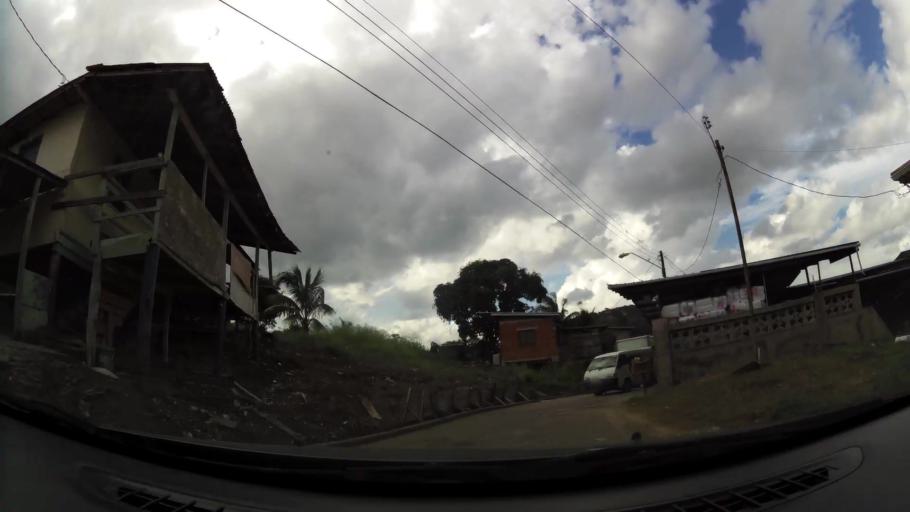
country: TT
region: City of San Fernando
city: Mon Repos
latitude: 10.2724
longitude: -61.4507
